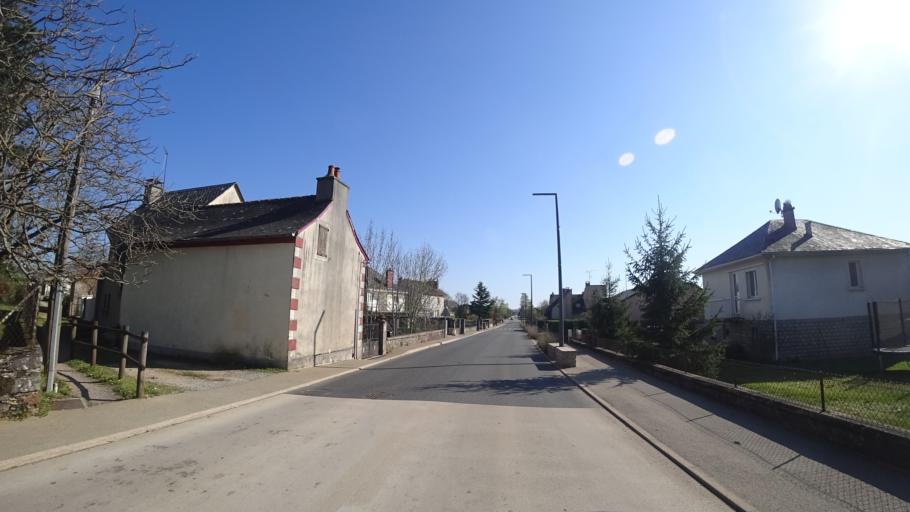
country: FR
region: Midi-Pyrenees
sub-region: Departement de l'Aveyron
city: Sebazac-Concoures
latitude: 44.4007
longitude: 2.5989
